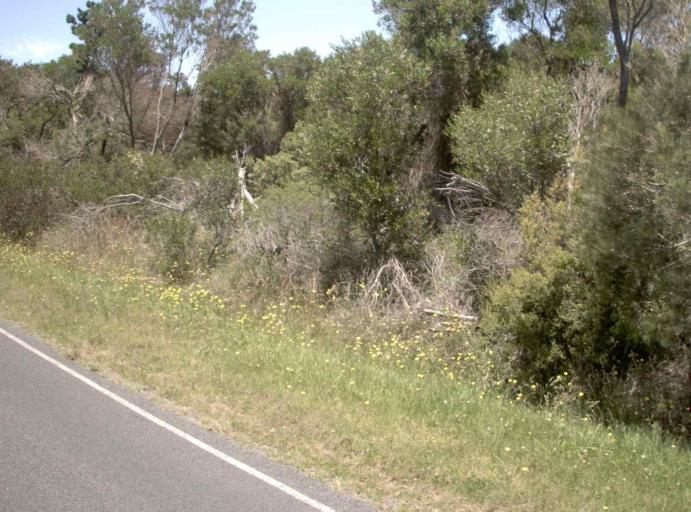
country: AU
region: Victoria
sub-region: Latrobe
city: Morwell
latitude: -38.7965
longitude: 146.1850
